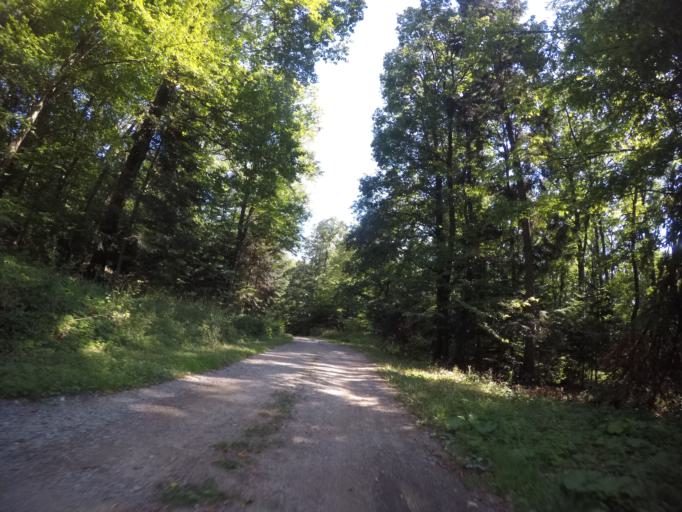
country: SK
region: Kosicky
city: Kosice
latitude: 48.7393
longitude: 21.1954
